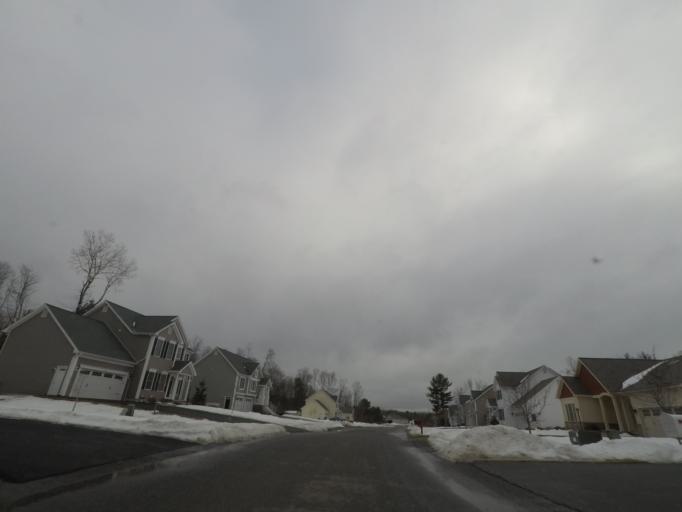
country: US
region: New York
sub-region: Schenectady County
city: Rotterdam
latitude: 42.7666
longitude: -73.9780
